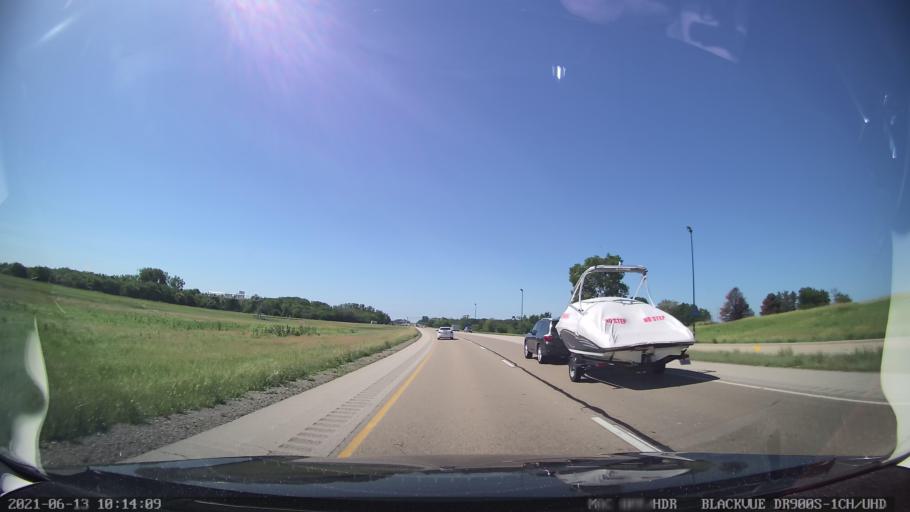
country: US
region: Illinois
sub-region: Logan County
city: Lincoln
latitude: 40.1745
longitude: -89.4180
